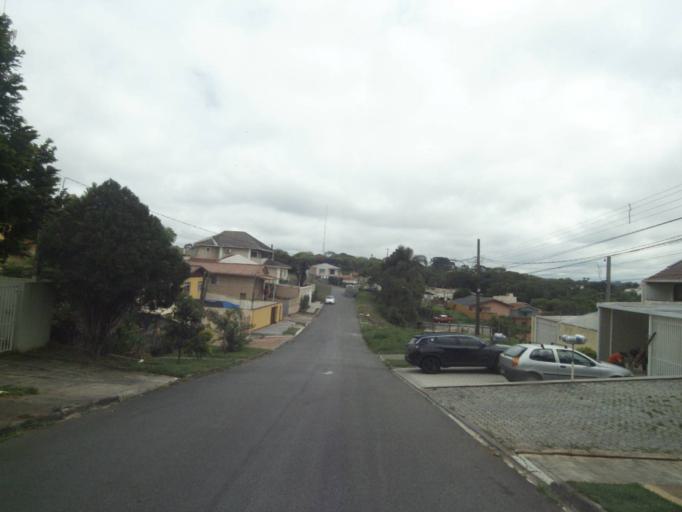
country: BR
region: Parana
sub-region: Curitiba
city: Curitiba
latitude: -25.3925
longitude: -49.2821
